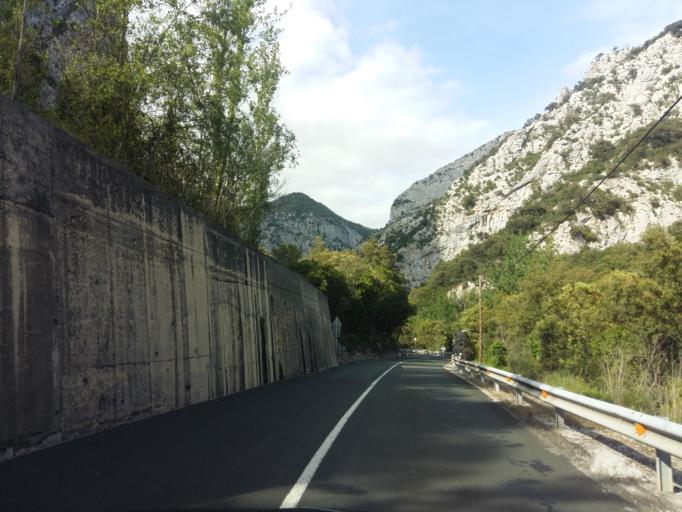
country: ES
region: Cantabria
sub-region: Provincia de Cantabria
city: Potes
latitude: 43.2222
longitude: -4.5872
